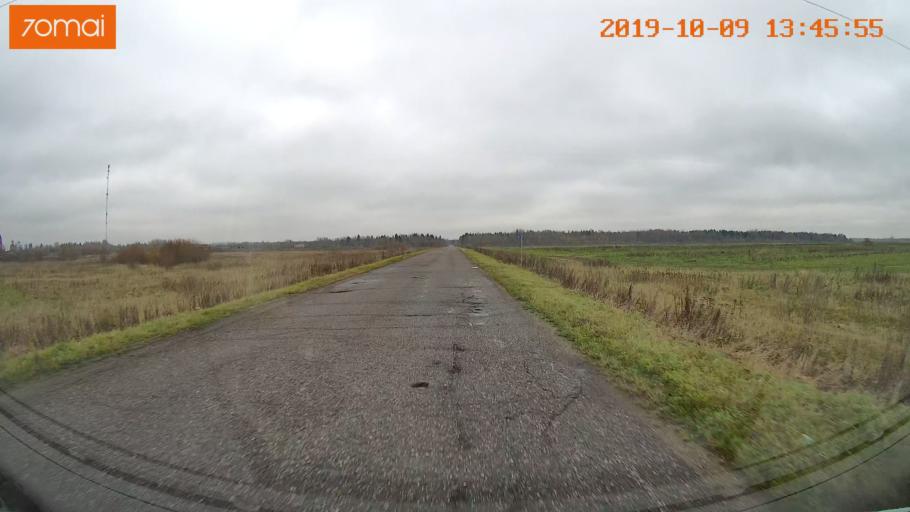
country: RU
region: Kostroma
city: Buy
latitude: 58.3788
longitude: 41.2139
